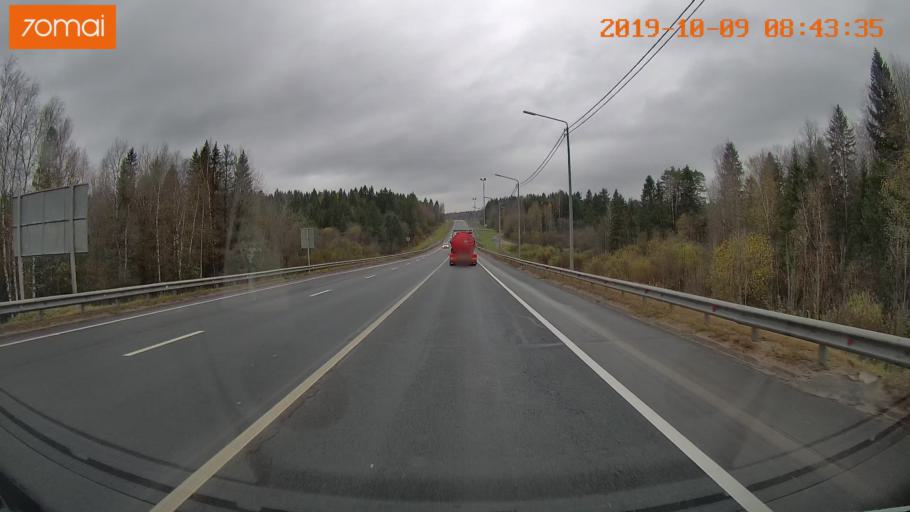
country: RU
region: Vologda
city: Gryazovets
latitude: 59.0255
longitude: 40.1137
